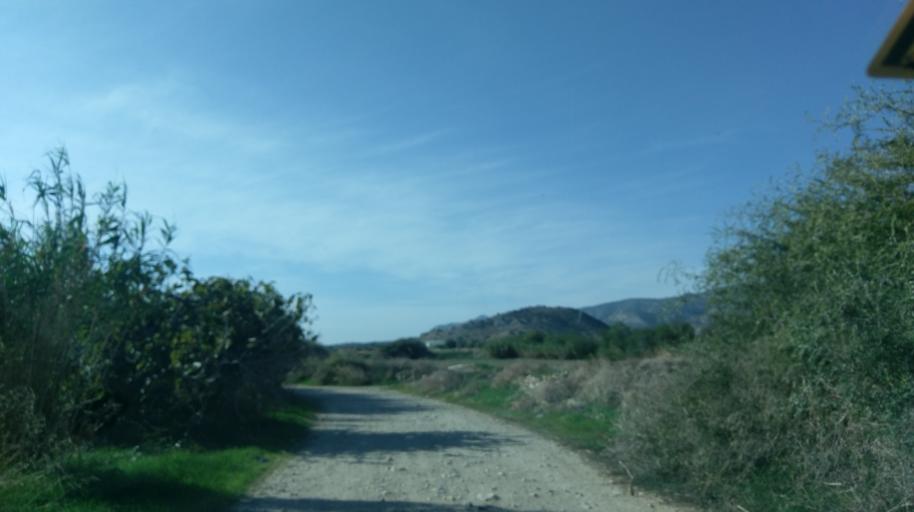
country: CY
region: Ammochostos
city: Trikomo
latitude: 35.3307
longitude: 33.8256
